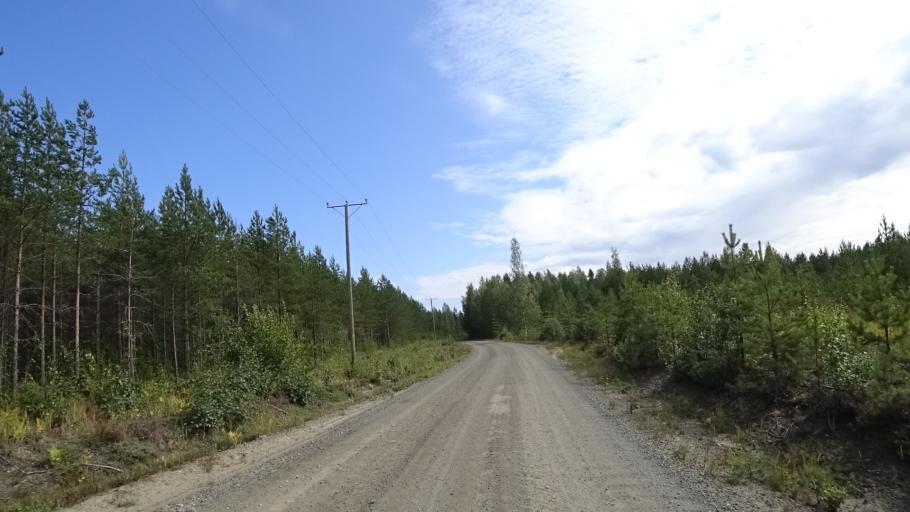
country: FI
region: North Karelia
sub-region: Joensuu
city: Pyhaeselkae
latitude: 62.3730
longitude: 29.8323
